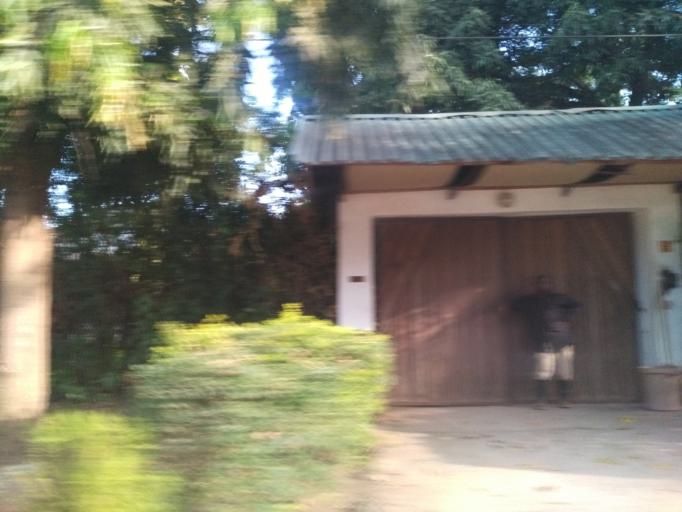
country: TZ
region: Dar es Salaam
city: Magomeni
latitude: -6.7811
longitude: 39.2708
